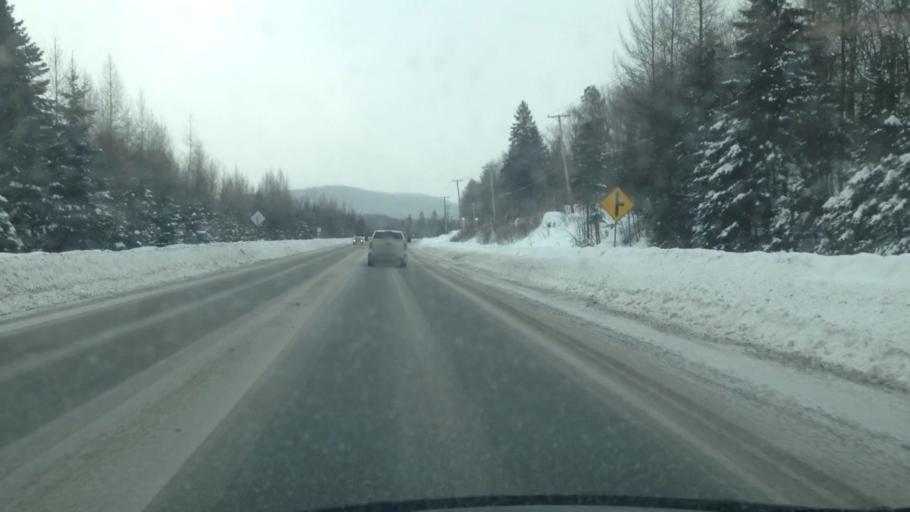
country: CA
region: Quebec
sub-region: Laurentides
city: Saint-Sauveur
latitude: 45.9000
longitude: -74.2213
